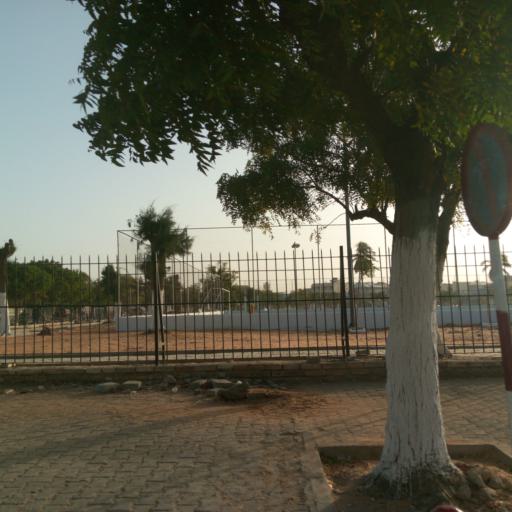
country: SN
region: Dakar
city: Dakar
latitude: 14.6947
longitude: -17.4494
